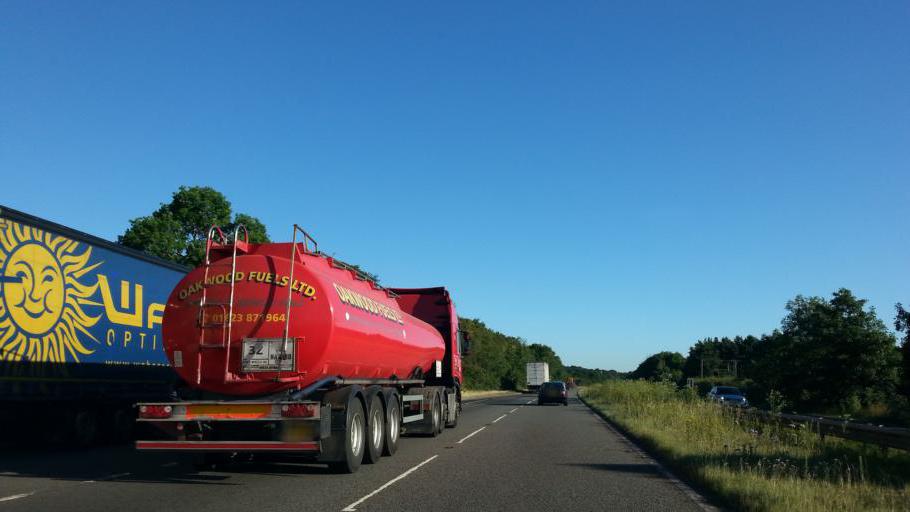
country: GB
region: England
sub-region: Nottinghamshire
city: Babworth
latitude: 53.3286
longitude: -1.0274
